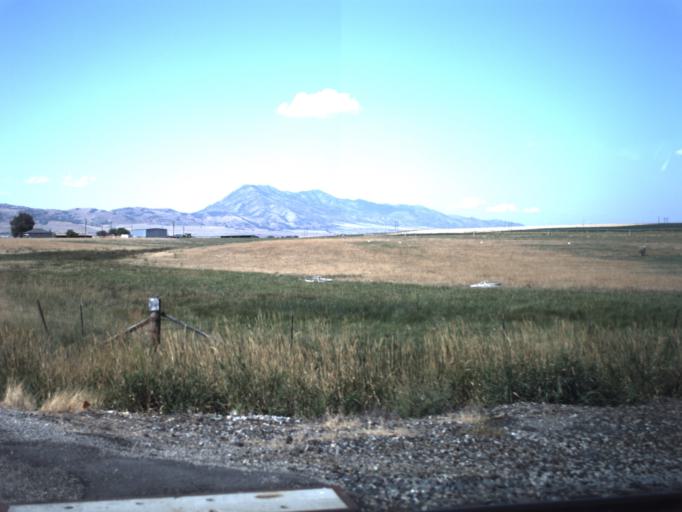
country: US
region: Utah
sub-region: Cache County
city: Benson
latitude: 41.8448
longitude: -111.9597
